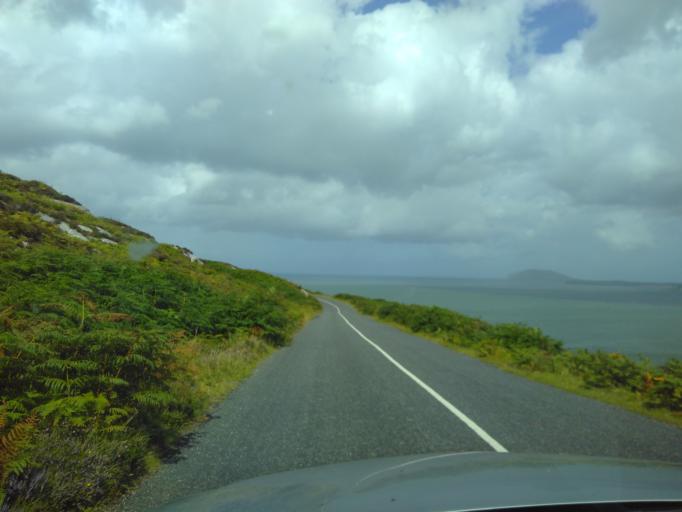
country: IE
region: Ulster
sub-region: County Donegal
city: Buncrana
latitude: 55.1832
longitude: -7.5866
